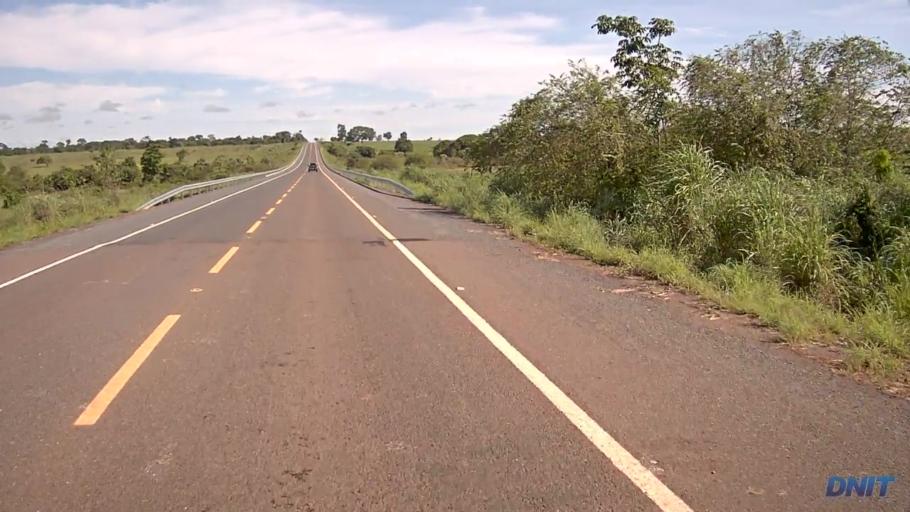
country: BR
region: Goias
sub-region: Sao Miguel Do Araguaia
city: Sao Miguel do Araguaia
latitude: -13.4549
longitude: -50.1194
